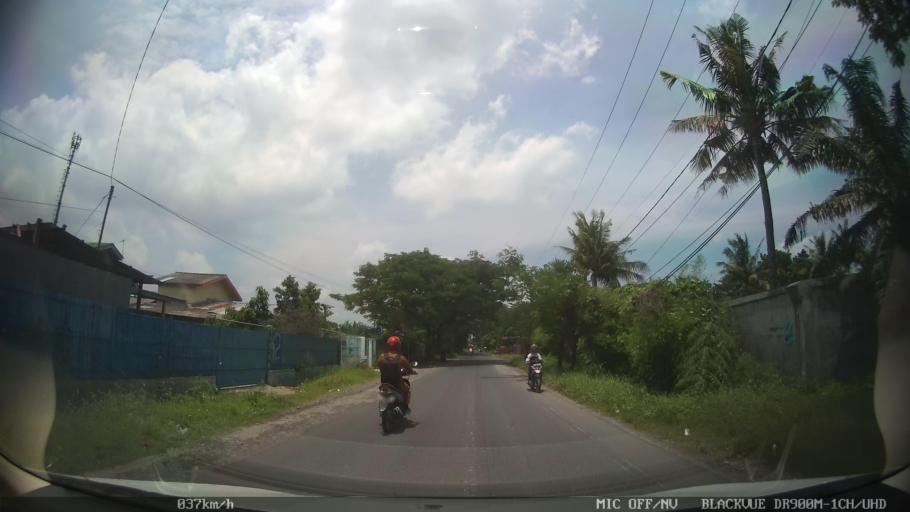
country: ID
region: North Sumatra
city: Labuhan Deli
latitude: 3.7093
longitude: 98.6711
